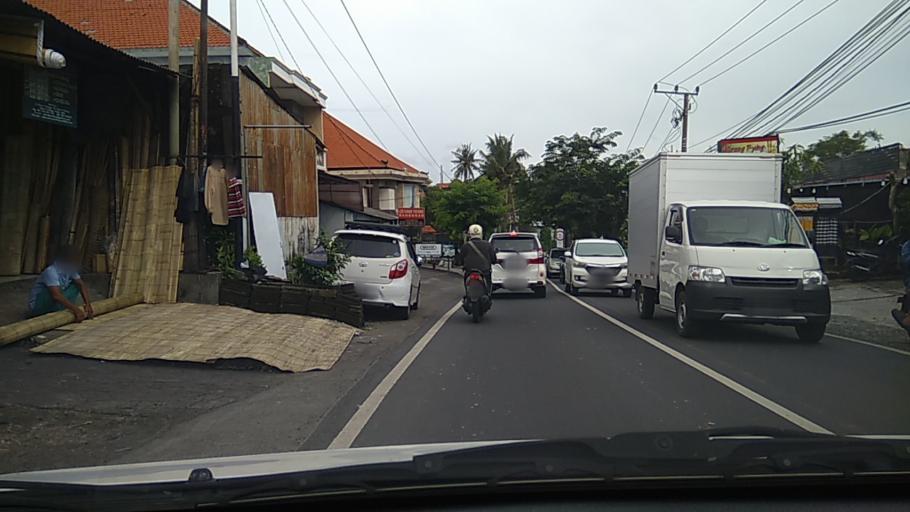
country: ID
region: Bali
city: Banjar Gunungpande
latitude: -8.6378
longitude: 115.1487
